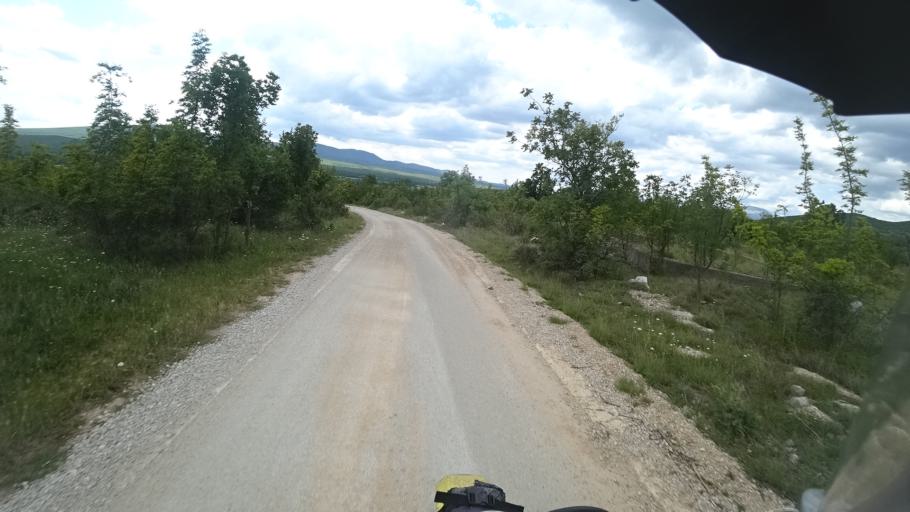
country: HR
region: Sibensko-Kniniska
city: Kistanje
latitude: 44.1080
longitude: 15.9543
